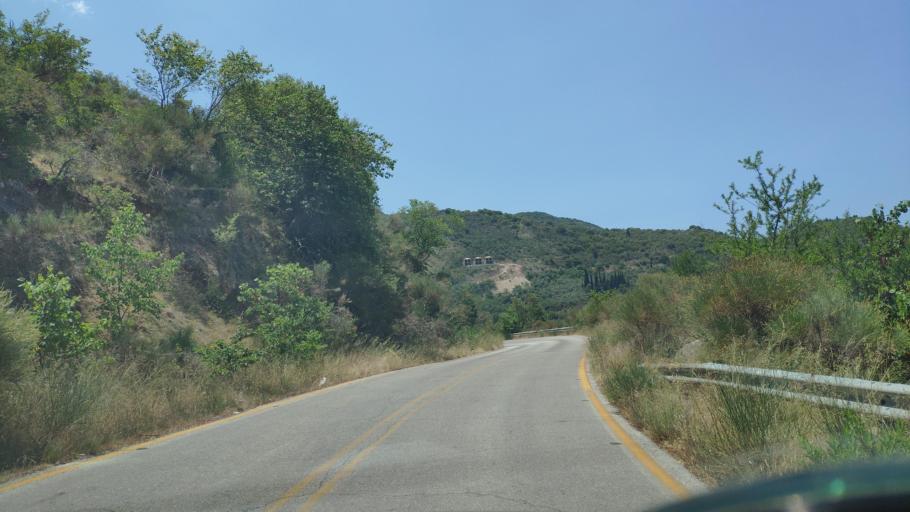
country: GR
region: Ionian Islands
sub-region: Lefkada
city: Nidri
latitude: 38.7492
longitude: 20.6208
